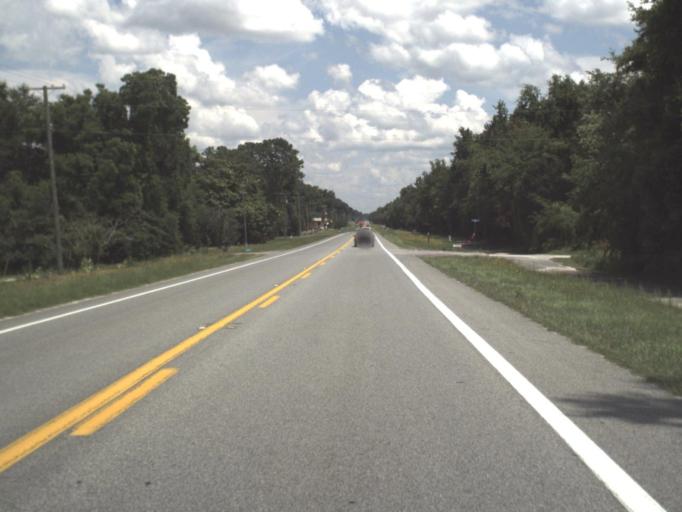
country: US
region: Florida
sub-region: Alachua County
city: High Springs
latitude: 29.9409
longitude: -82.7398
